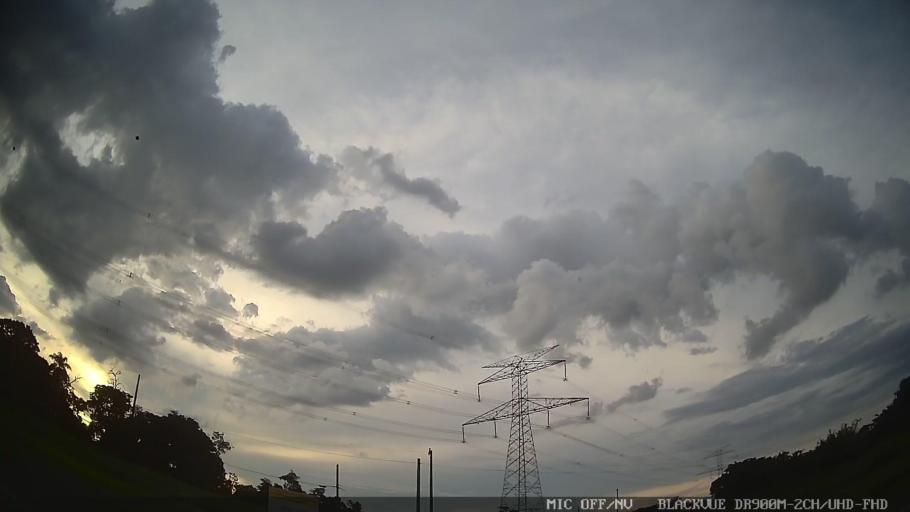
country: BR
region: Sao Paulo
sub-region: Campinas
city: Campinas
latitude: -22.8074
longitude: -47.0335
